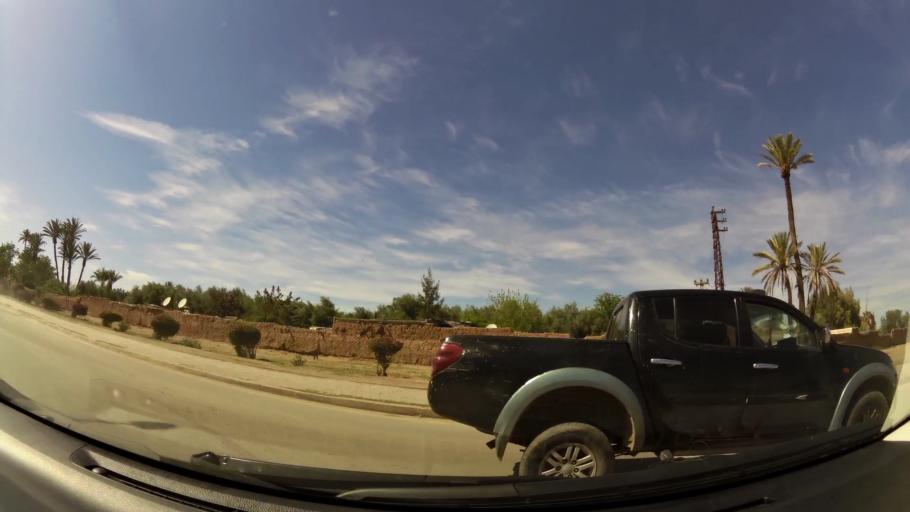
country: MA
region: Marrakech-Tensift-Al Haouz
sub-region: Marrakech
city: Marrakesh
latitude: 31.6255
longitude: -7.9634
